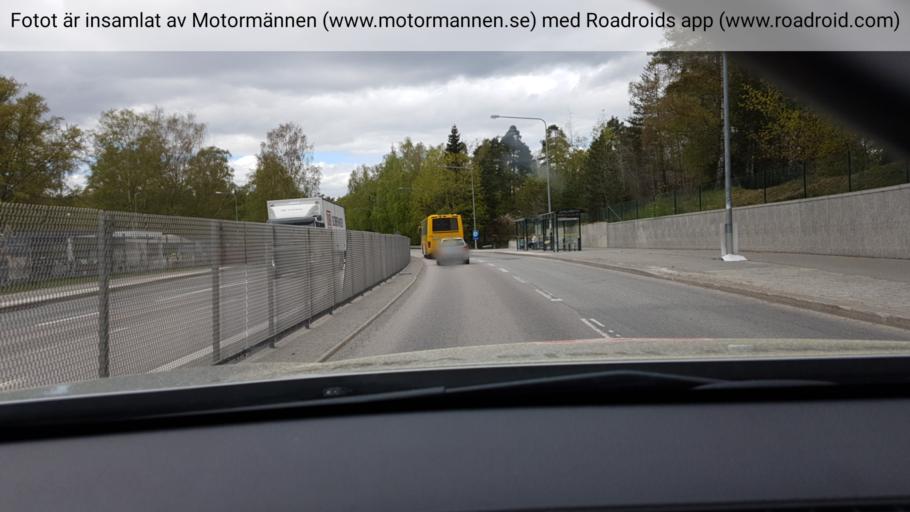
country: SE
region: Stockholm
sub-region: Tyreso Kommun
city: Bollmora
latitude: 59.2286
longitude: 18.1999
